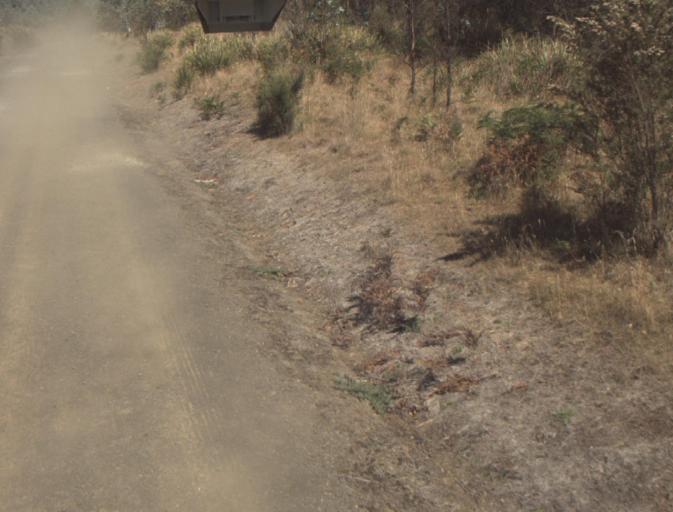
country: AU
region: Tasmania
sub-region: Dorset
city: Scottsdale
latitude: -41.3172
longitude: 147.3826
